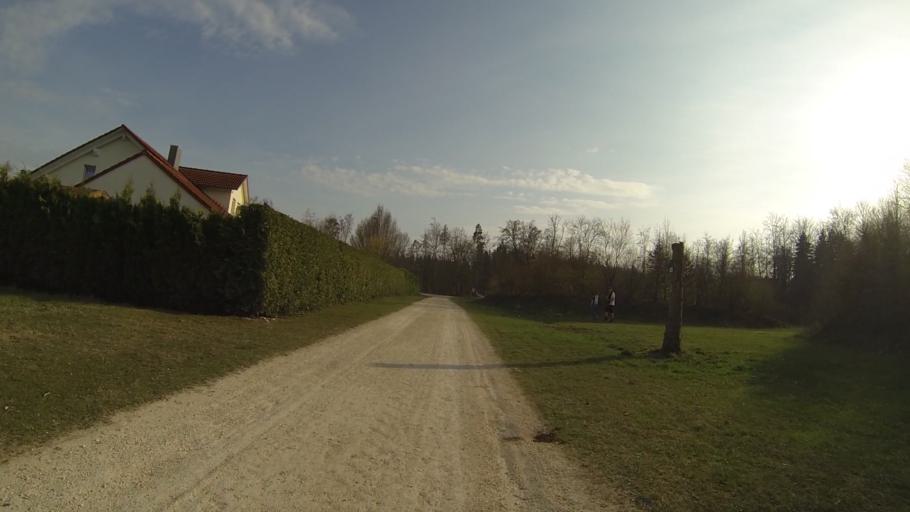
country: DE
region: Baden-Wuerttemberg
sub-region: Regierungsbezirk Stuttgart
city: Heidenheim an der Brenz
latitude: 48.6574
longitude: 10.1334
